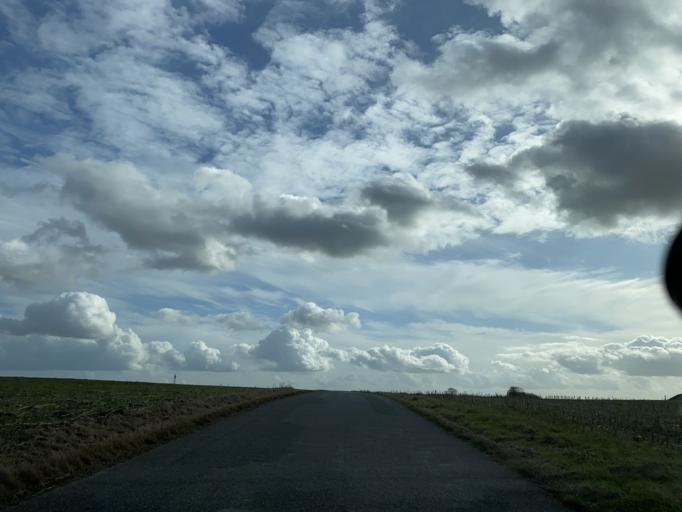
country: DK
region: Central Jutland
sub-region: Arhus Kommune
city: Sabro
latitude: 56.2049
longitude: 9.9924
